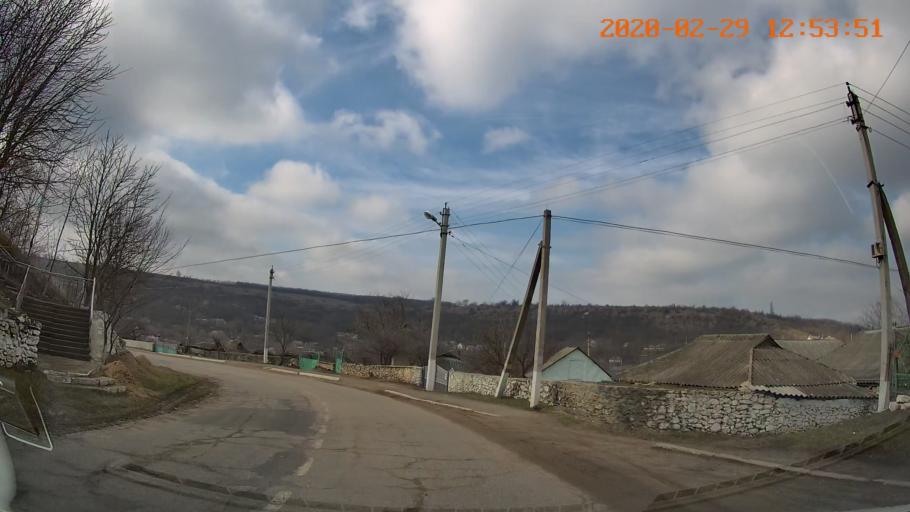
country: MD
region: Telenesti
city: Camenca
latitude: 48.1056
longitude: 28.7310
